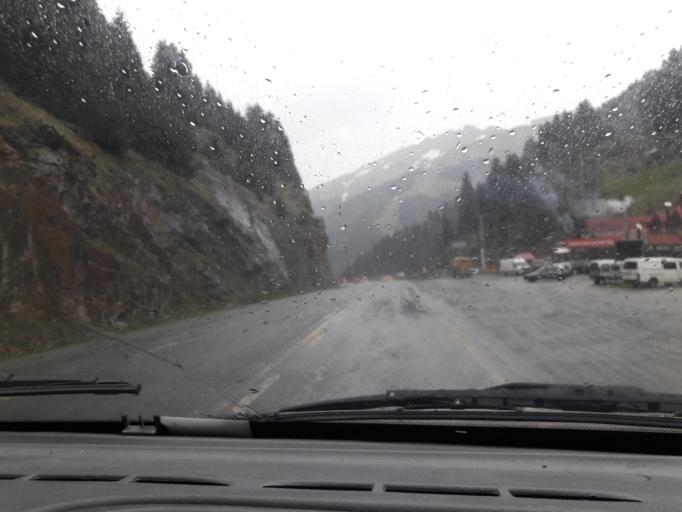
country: TR
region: Gumushane
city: Yaglidere
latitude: 40.6745
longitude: 39.4255
